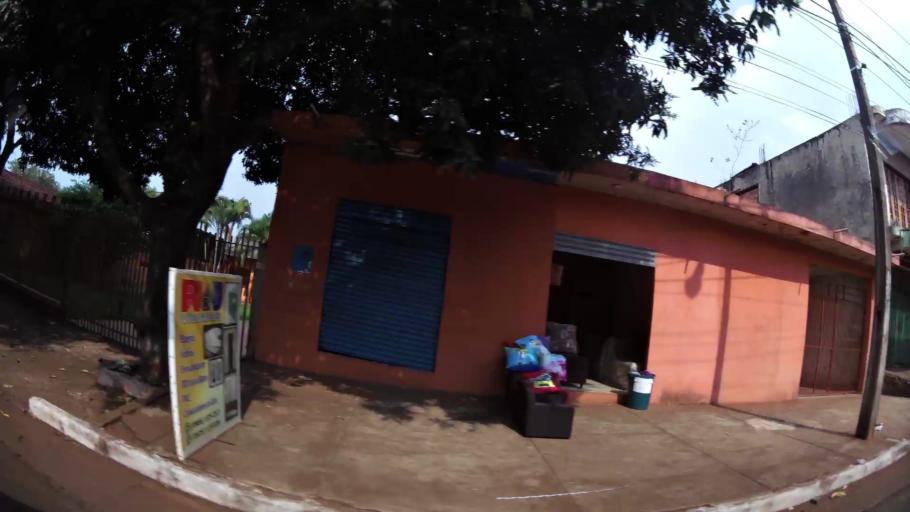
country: PY
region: Alto Parana
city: Ciudad del Este
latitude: -25.4942
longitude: -54.6494
